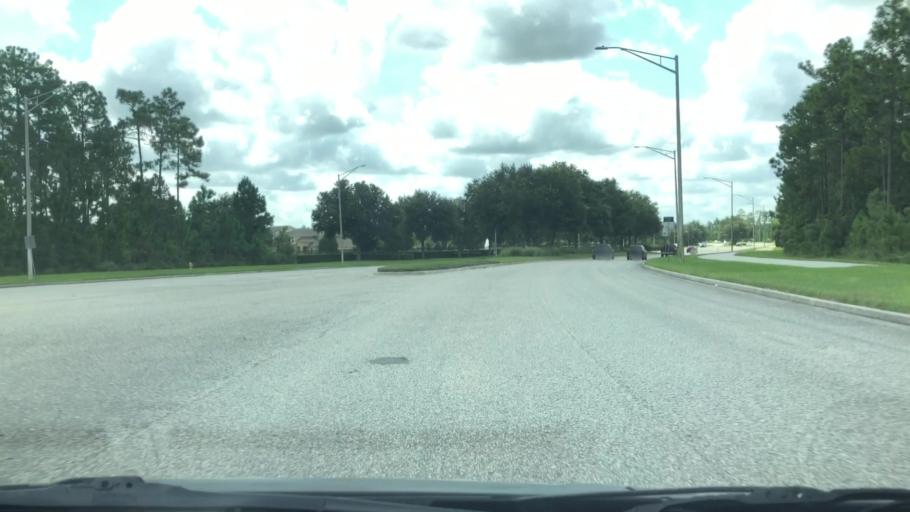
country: US
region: Florida
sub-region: Saint Johns County
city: Fruit Cove
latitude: 30.1350
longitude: -81.5449
